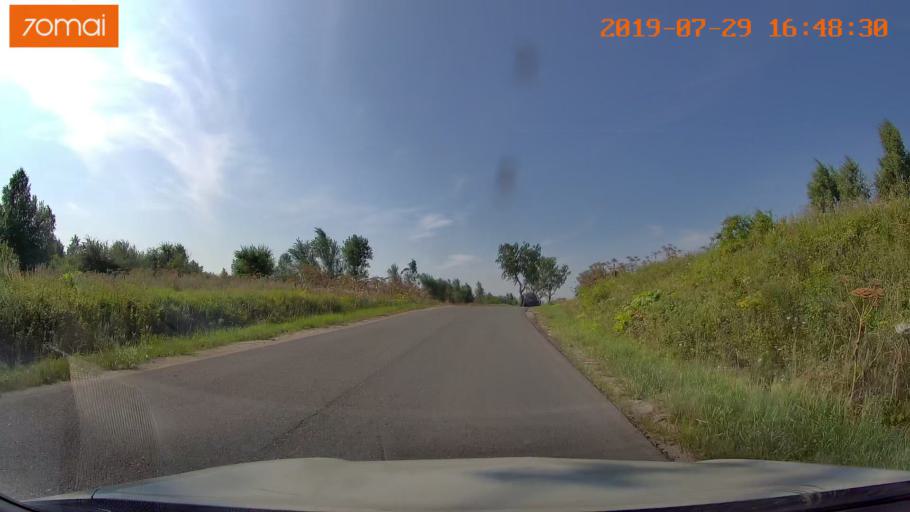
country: RU
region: Kaliningrad
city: Primorsk
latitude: 54.7872
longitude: 20.0763
